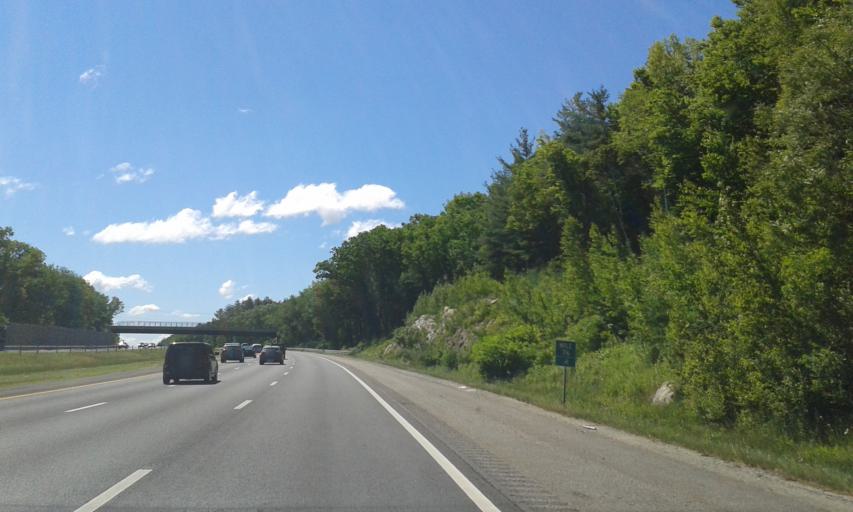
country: US
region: Massachusetts
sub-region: Middlesex County
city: Billerica
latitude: 42.5318
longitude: -71.2764
